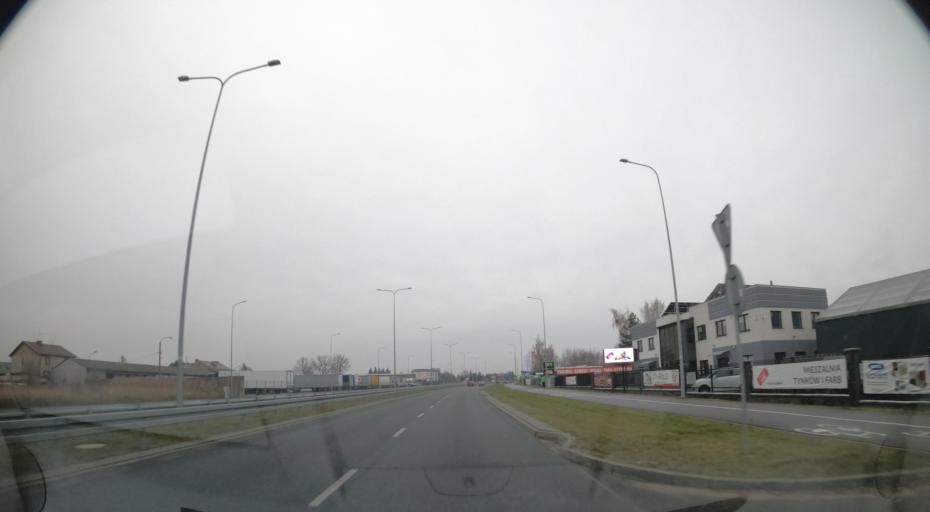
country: PL
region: Masovian Voivodeship
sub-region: Radom
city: Radom
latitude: 51.3909
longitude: 21.1941
